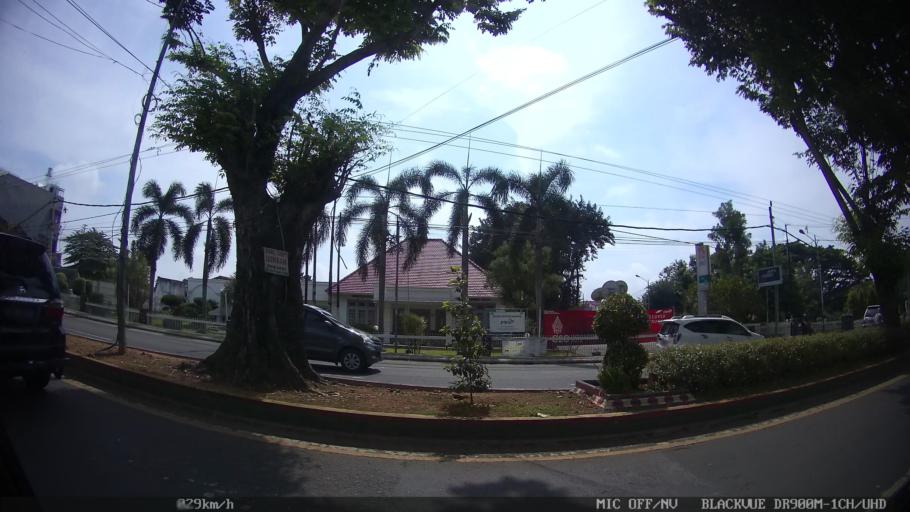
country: ID
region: Lampung
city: Kedaton
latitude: -5.3849
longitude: 105.2608
